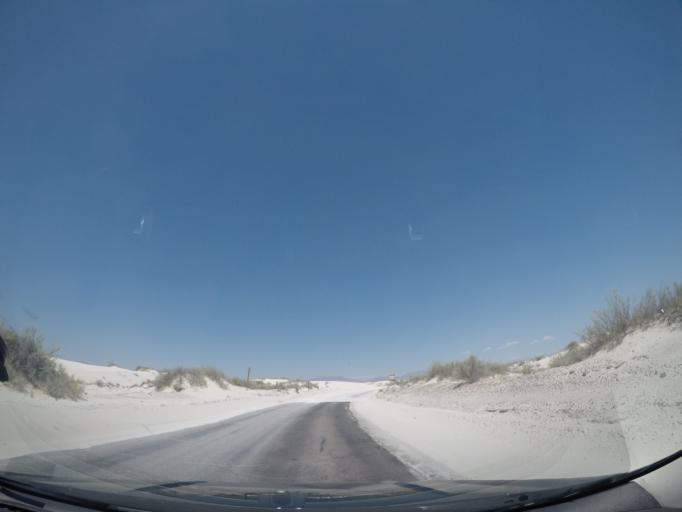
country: US
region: New Mexico
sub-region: Otero County
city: Holloman Air Force Base
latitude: 32.7954
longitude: -106.2440
